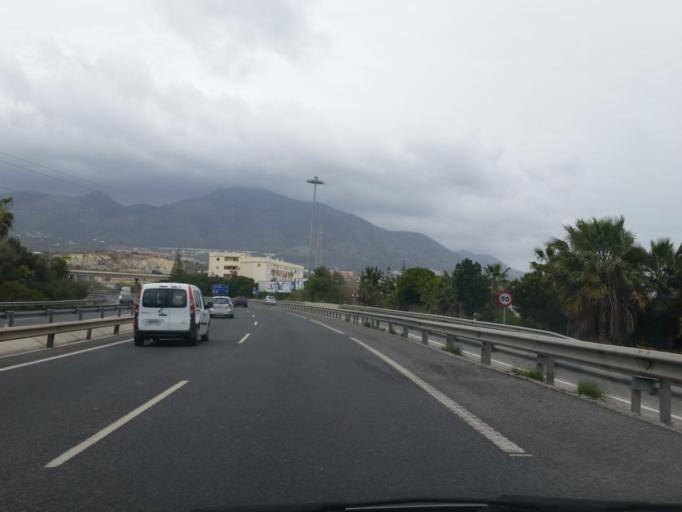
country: ES
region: Andalusia
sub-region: Provincia de Malaga
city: Fuengirola
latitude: 36.5559
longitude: -4.6206
